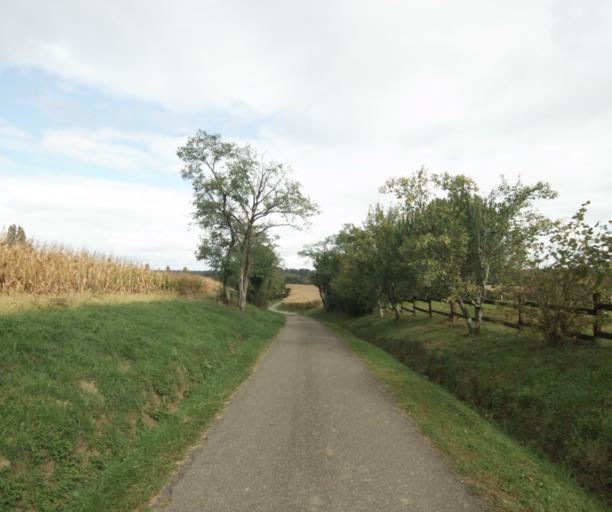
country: FR
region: Midi-Pyrenees
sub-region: Departement du Gers
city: Nogaro
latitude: 43.8514
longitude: -0.0132
